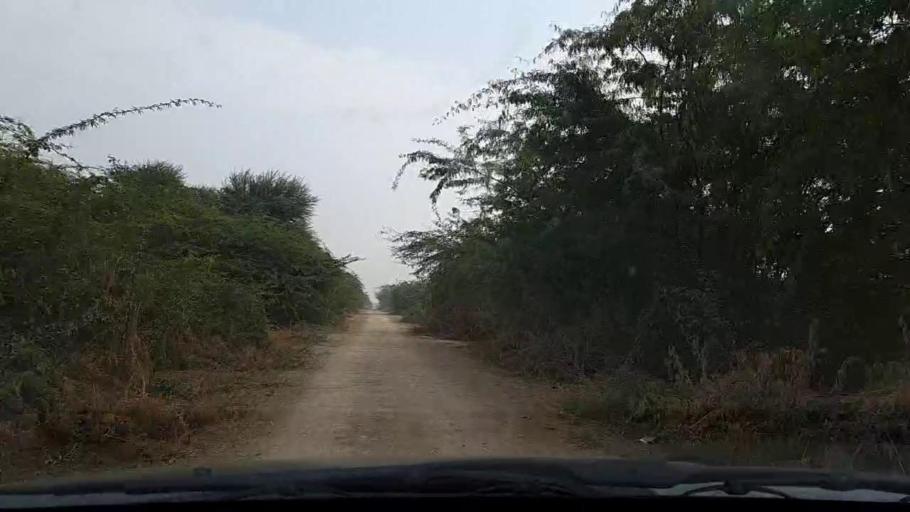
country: PK
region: Sindh
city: Pithoro
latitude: 25.7090
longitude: 69.3844
